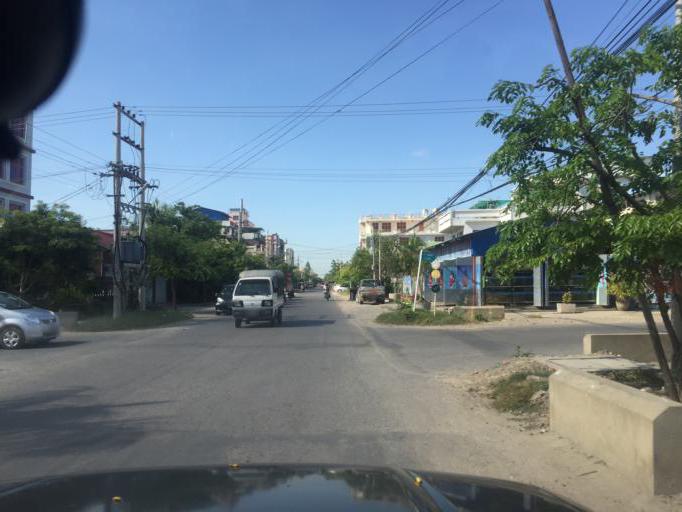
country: MM
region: Mandalay
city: Mandalay
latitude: 21.9570
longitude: 96.1099
